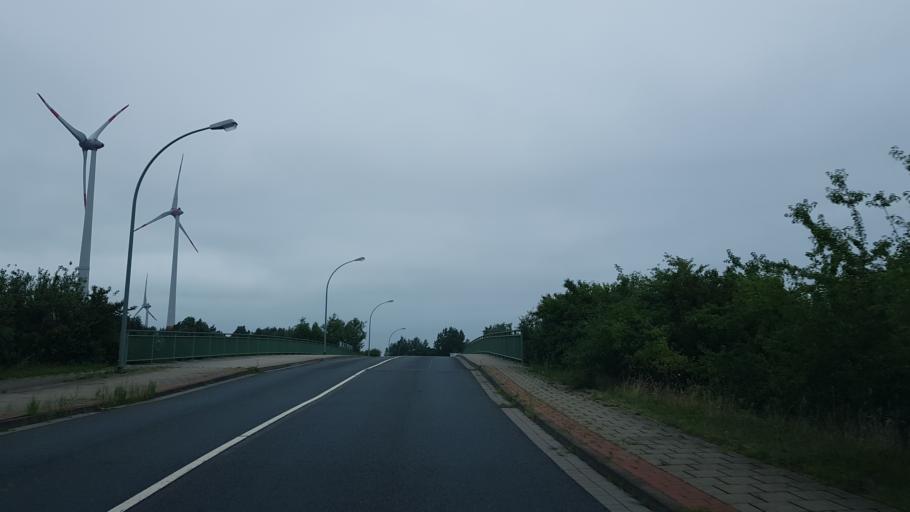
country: DE
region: Lower Saxony
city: Langen
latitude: 53.5865
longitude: 8.5614
